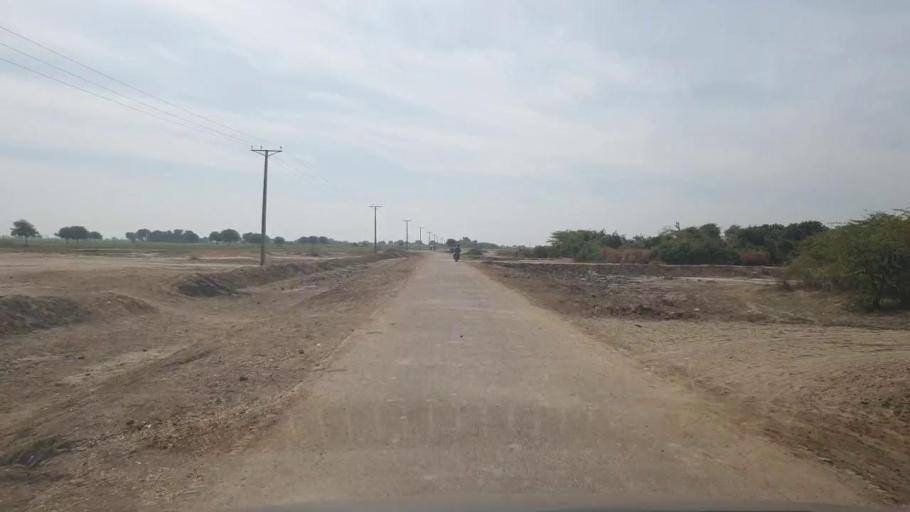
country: PK
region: Sindh
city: Umarkot
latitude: 25.3304
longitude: 69.5935
